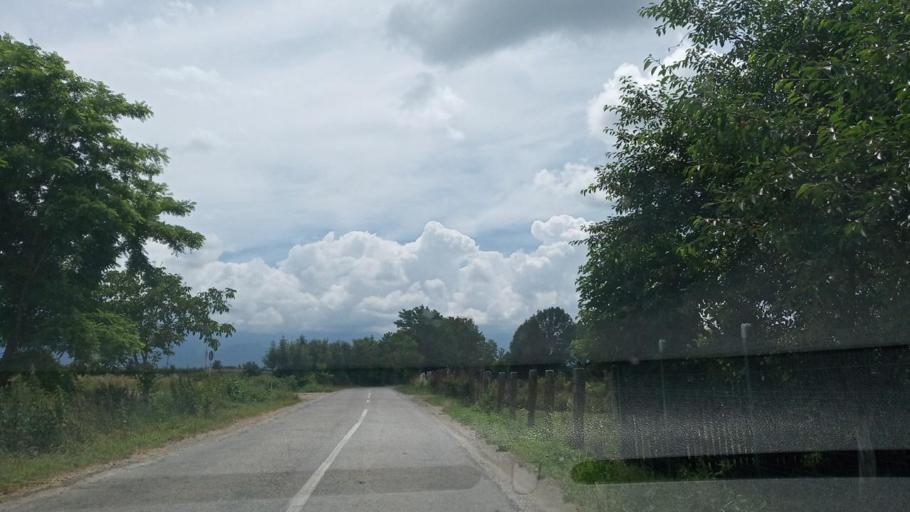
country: RO
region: Sibiu
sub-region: Comuna Porumbacu de Jos
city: Porumbacu de Jos
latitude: 45.7533
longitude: 24.4611
